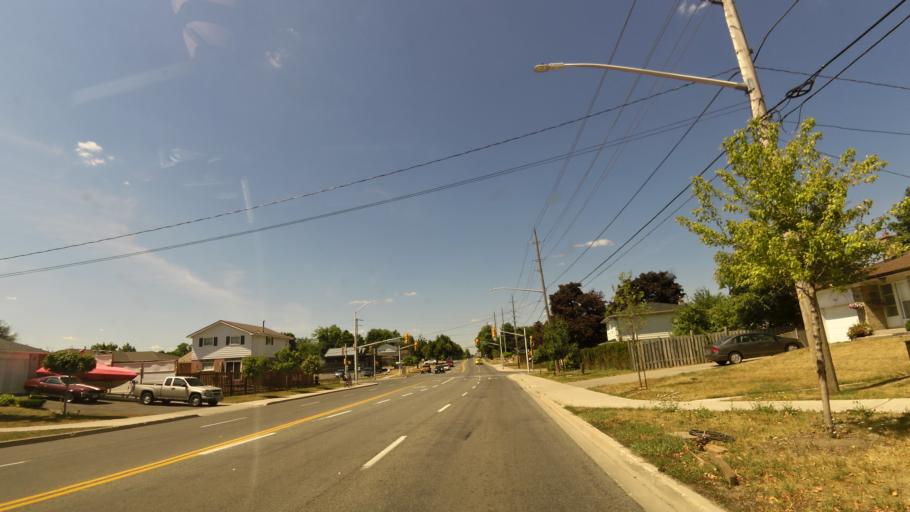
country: CA
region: Ontario
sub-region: Halton
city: Milton
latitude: 43.6421
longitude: -79.8924
